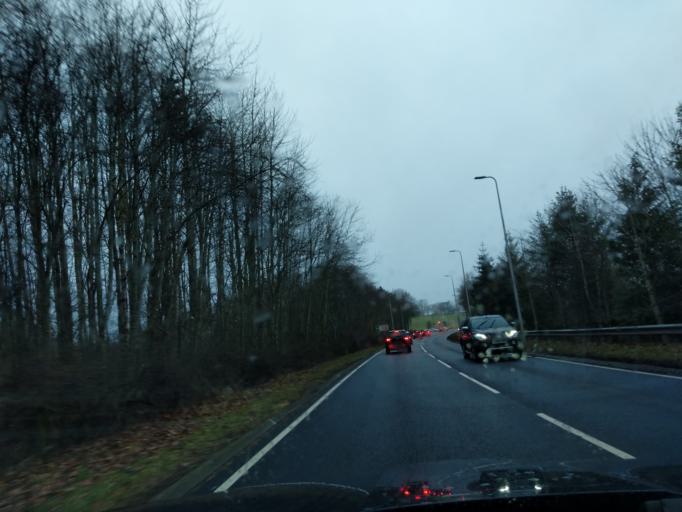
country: GB
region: Scotland
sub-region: The Scottish Borders
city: Melrose
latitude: 55.5974
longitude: -2.7416
